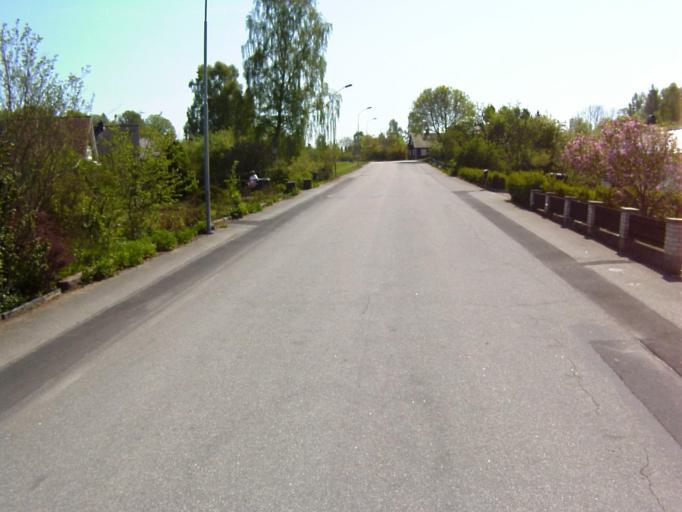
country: SE
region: Skane
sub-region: Kristianstads Kommun
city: Tollarp
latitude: 56.1685
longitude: 14.2896
